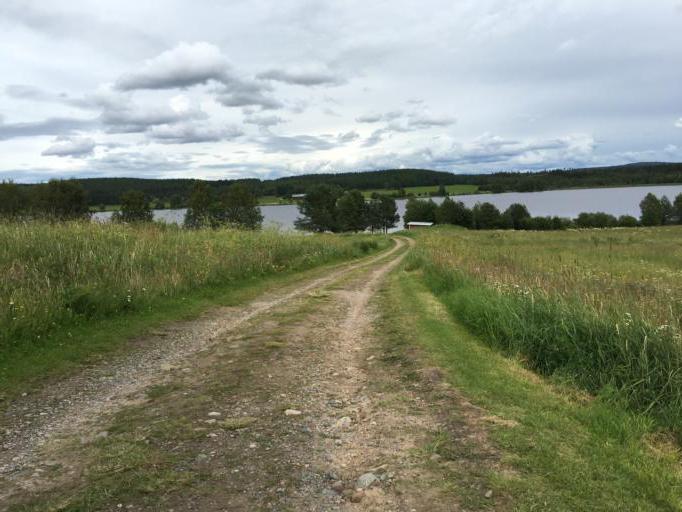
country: SE
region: Norrbotten
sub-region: Overkalix Kommun
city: OEverkalix
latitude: 66.1095
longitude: 22.7879
